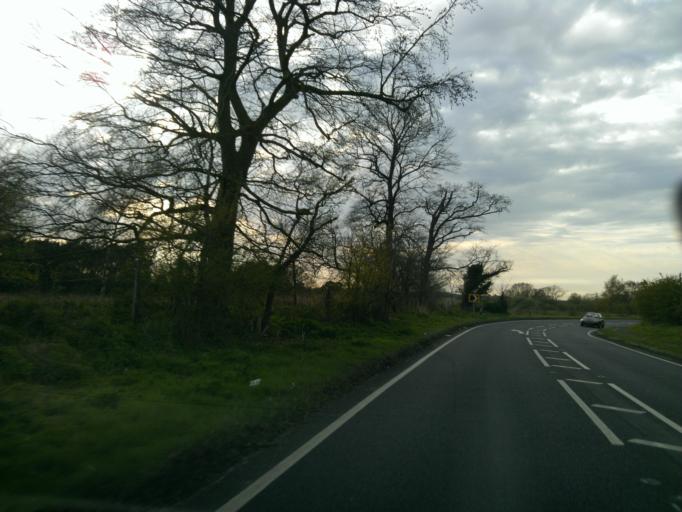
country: GB
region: England
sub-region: Essex
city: Saint Osyth
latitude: 51.8083
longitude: 1.0751
